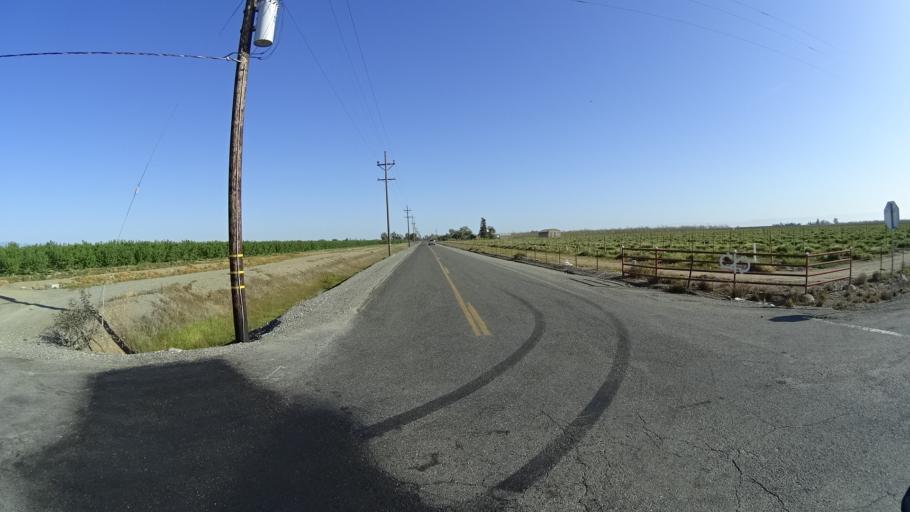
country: US
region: California
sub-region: Glenn County
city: Orland
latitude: 39.6821
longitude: -122.1781
